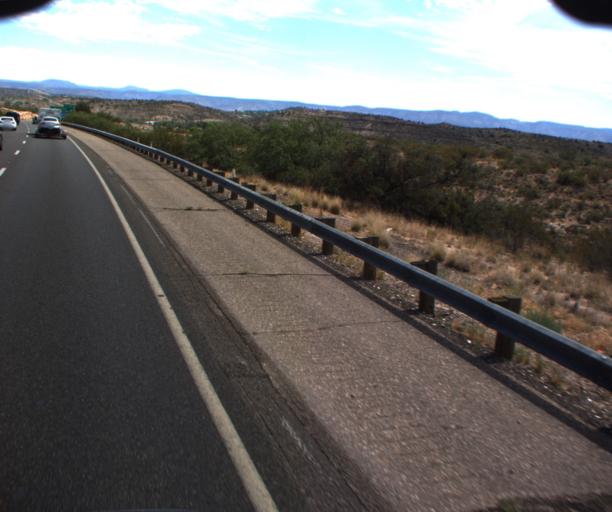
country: US
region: Arizona
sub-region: Yavapai County
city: Lake Montezuma
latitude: 34.6363
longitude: -111.8238
